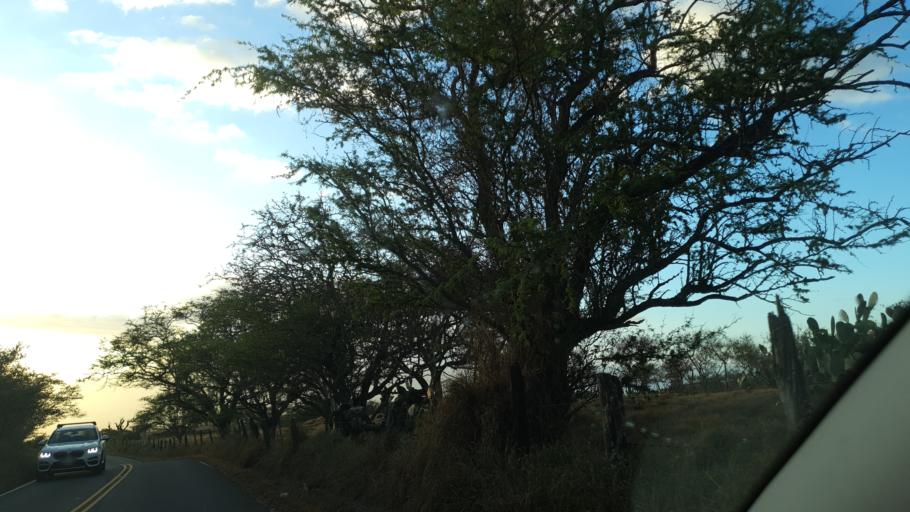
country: US
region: Hawaii
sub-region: Maui County
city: Pukalani
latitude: 20.7839
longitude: -156.3458
